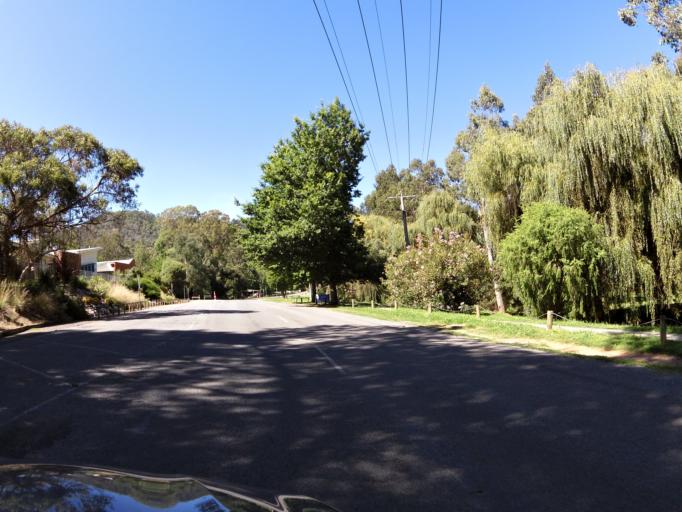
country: AU
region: Victoria
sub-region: Alpine
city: Mount Beauty
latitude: -36.7319
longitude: 146.9607
